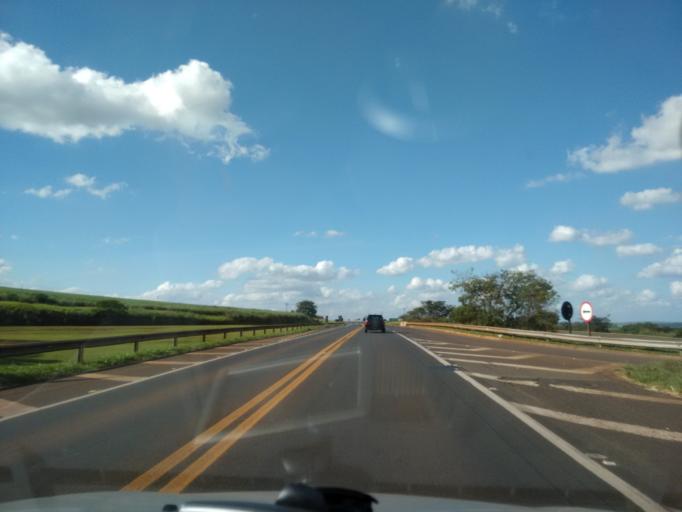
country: BR
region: Sao Paulo
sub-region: Americo Brasiliense
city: Americo Brasiliense
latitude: -21.7556
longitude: -48.0701
